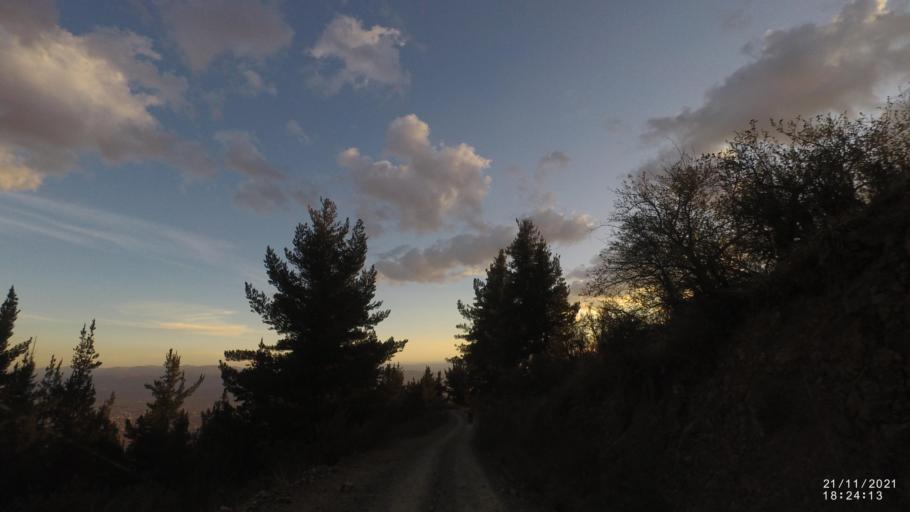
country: BO
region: Cochabamba
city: Cochabamba
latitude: -17.2999
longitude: -66.2180
